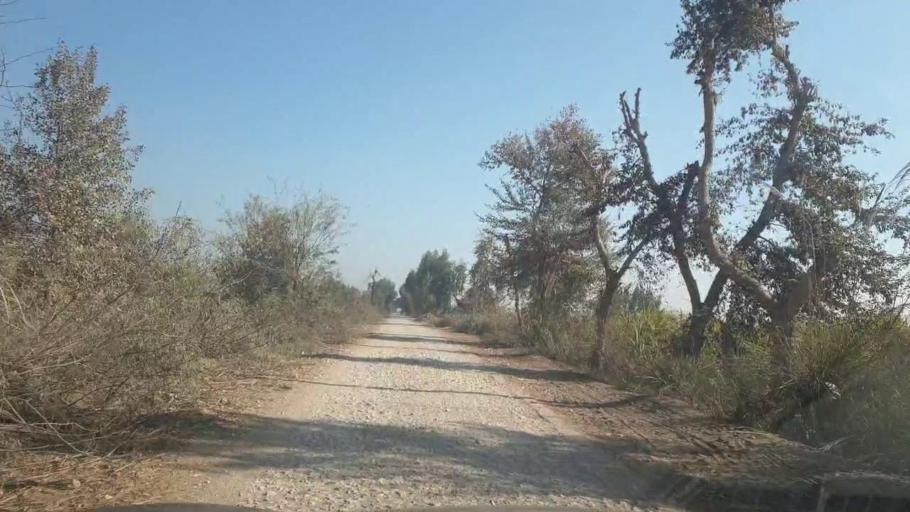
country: PK
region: Sindh
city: Mirpur Mathelo
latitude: 28.1109
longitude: 69.4751
